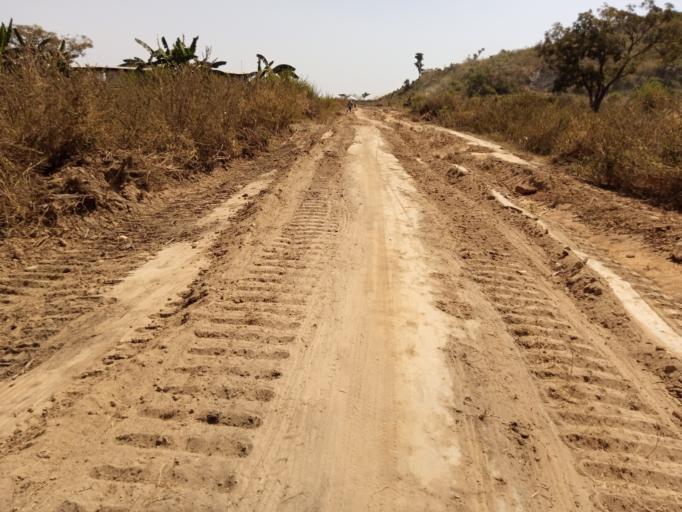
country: NG
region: Abuja Federal Capital Territory
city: Kuje
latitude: 8.9053
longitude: 7.3374
